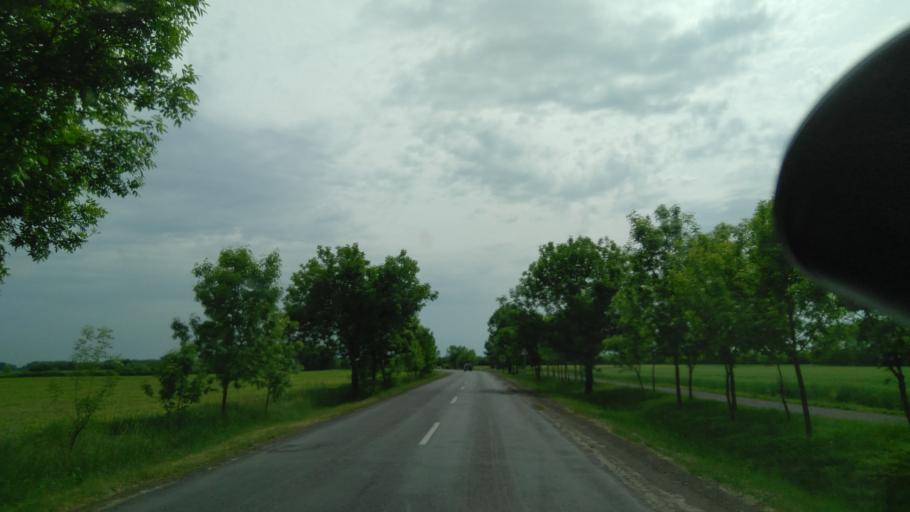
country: HU
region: Bekes
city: Sarkad
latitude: 46.7967
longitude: 21.3814
